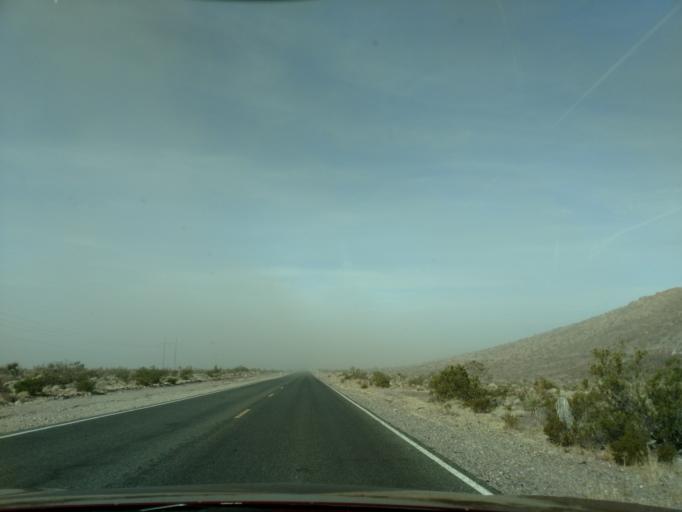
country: US
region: Nevada
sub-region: Nye County
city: Pahrump
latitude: 36.4411
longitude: -116.0907
